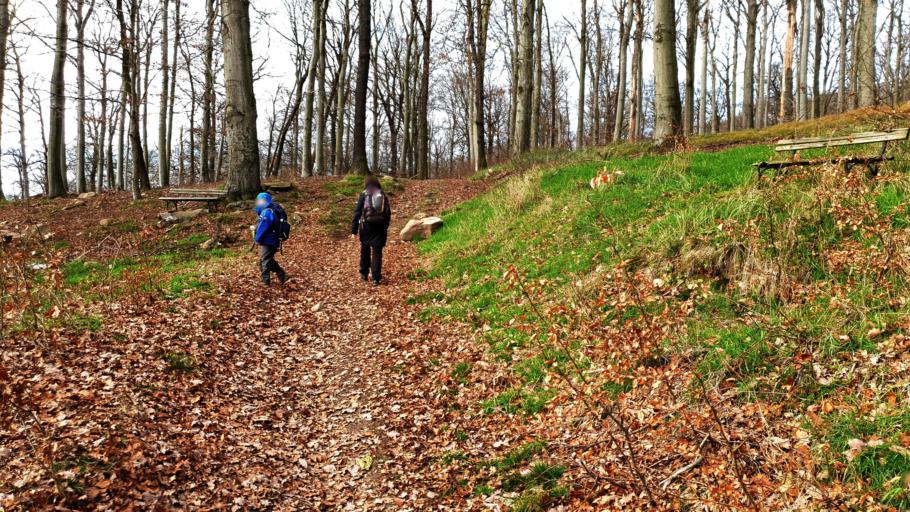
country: DE
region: Saxony
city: Hohburg
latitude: 51.4175
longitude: 12.7992
